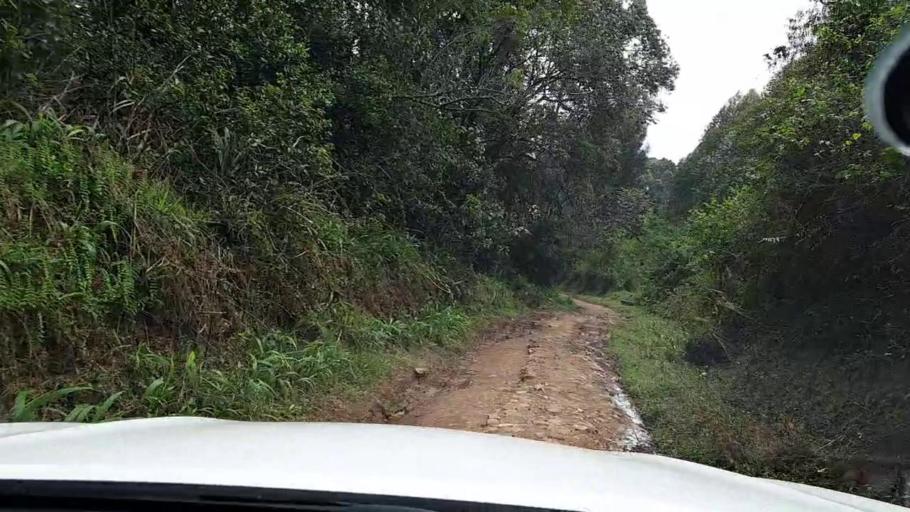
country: RW
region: Western Province
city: Kibuye
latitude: -2.2831
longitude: 29.3049
